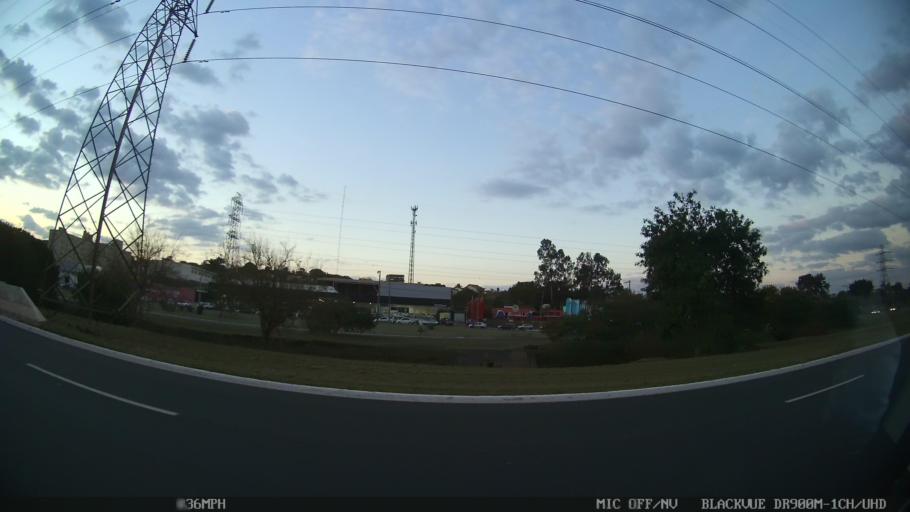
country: BR
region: Sao Paulo
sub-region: Ribeirao Preto
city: Ribeirao Preto
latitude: -21.2112
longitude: -47.7779
